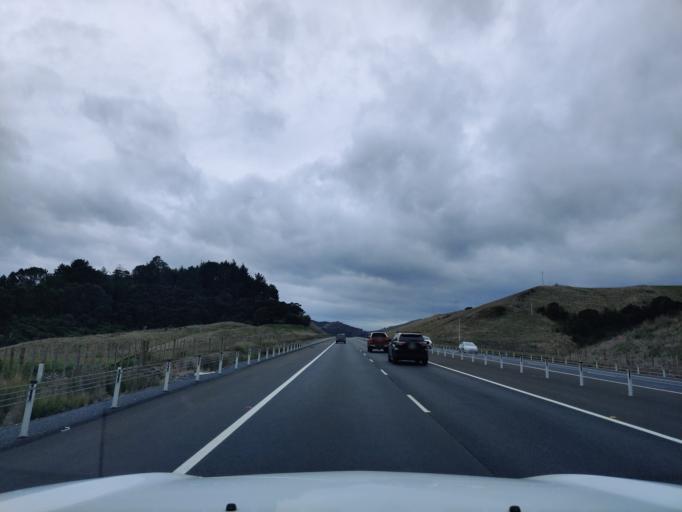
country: NZ
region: Waikato
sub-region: Waikato District
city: Ngaruawahia
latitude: -37.5459
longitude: 175.1896
